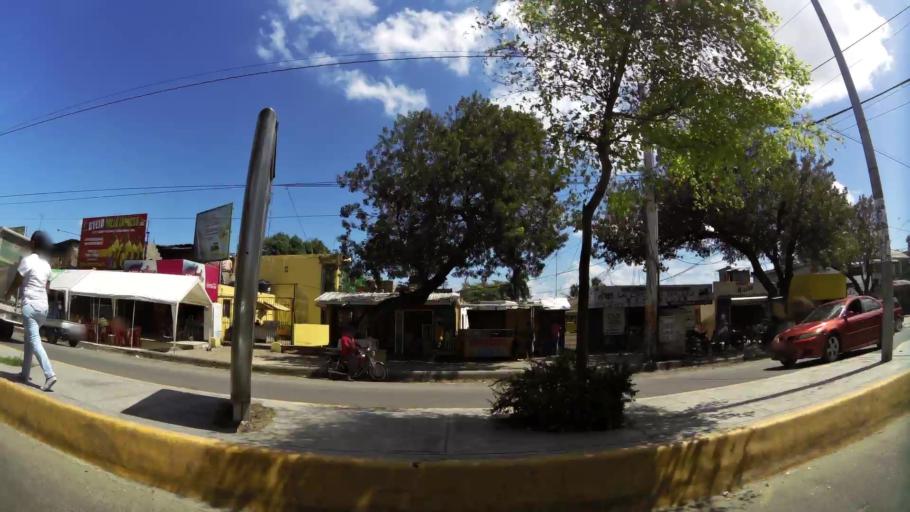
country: DO
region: San Cristobal
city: San Cristobal
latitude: 18.4155
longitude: -70.1070
